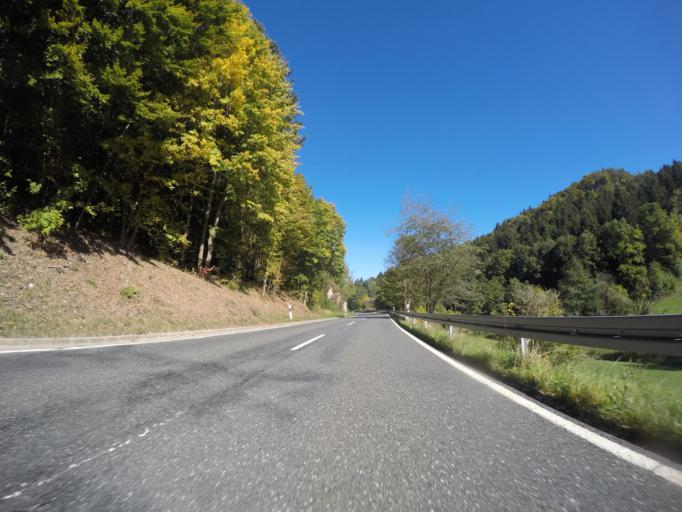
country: DE
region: Bavaria
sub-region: Upper Franconia
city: Gossweinstein
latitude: 49.8031
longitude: 11.3323
